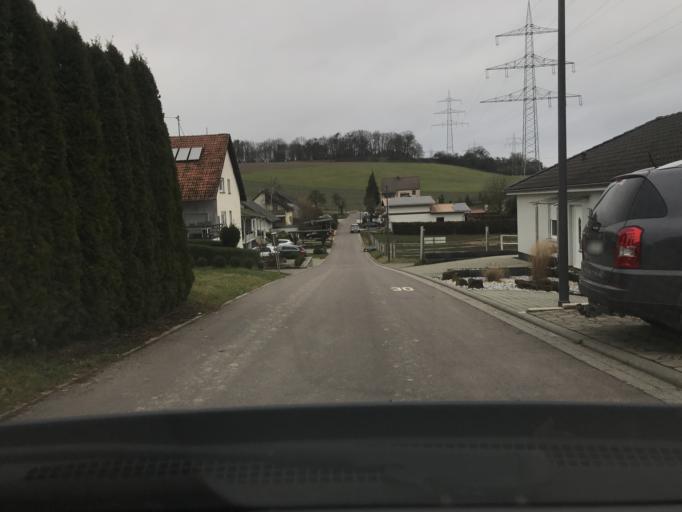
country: DE
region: Rheinland-Pfalz
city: Newel
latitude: 49.7905
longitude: 6.5699
